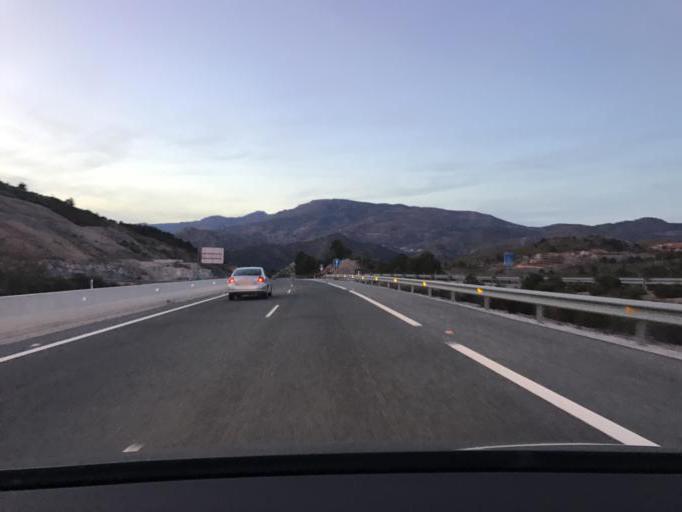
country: ES
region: Andalusia
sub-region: Provincia de Granada
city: Velez de Benaudalla
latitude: 36.8064
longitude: -3.5108
